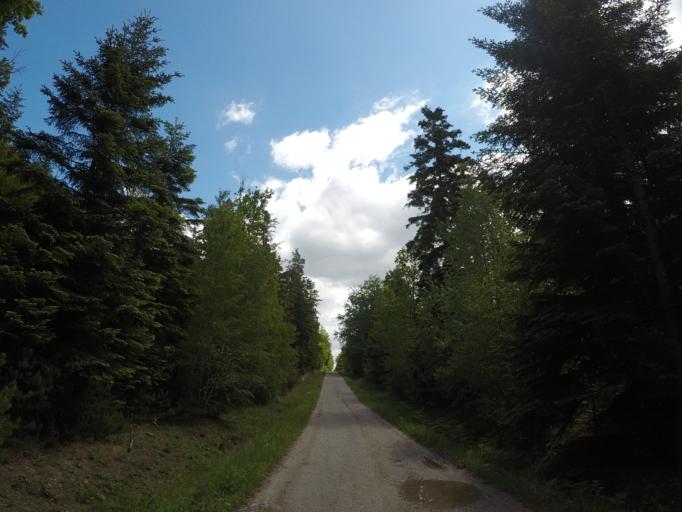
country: PL
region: Swietokrzyskie
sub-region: Powiat kielecki
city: Kielce
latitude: 50.9167
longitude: 20.6441
